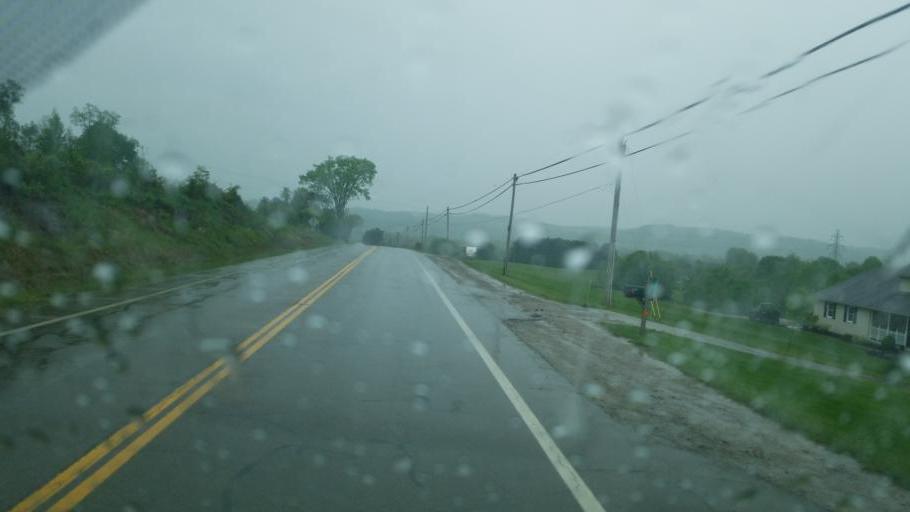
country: US
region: Ohio
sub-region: Muskingum County
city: Dresden
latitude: 40.1058
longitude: -82.0280
